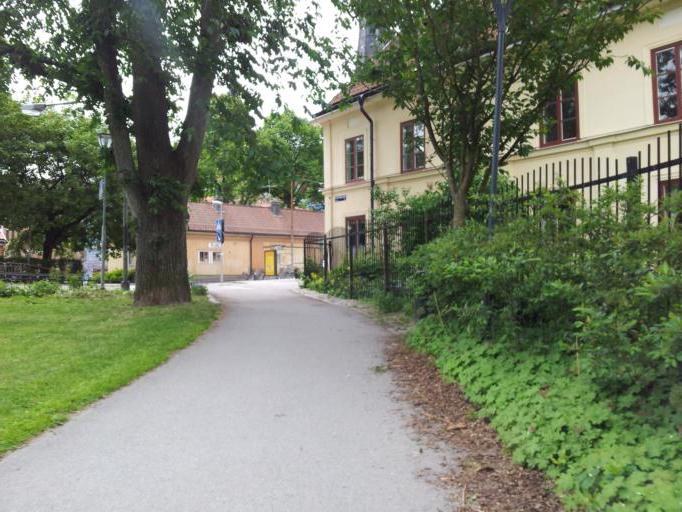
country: SE
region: Uppsala
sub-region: Uppsala Kommun
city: Uppsala
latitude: 59.8600
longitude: 17.6324
